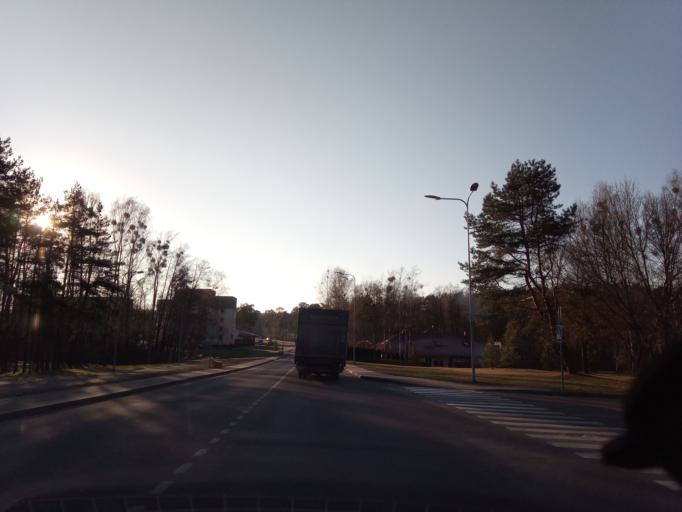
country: LT
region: Alytaus apskritis
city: Druskininkai
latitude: 54.0068
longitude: 23.9855
